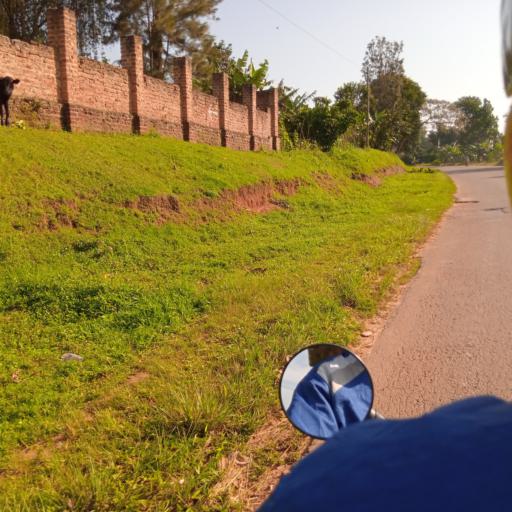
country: UG
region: Central Region
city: Masaka
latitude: -0.4504
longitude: 31.6684
